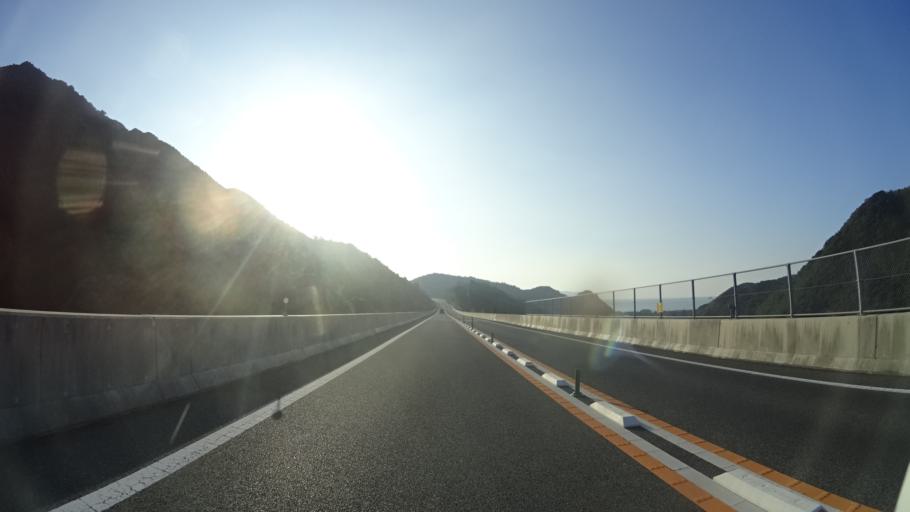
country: JP
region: Yamaguchi
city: Hagi
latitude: 34.3874
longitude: 131.3400
